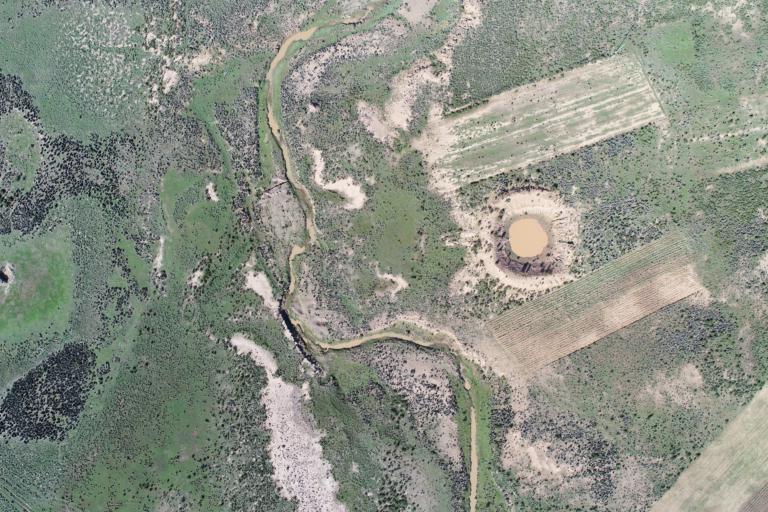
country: BO
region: La Paz
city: Curahuara de Carangas
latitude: -17.3037
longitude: -68.5236
